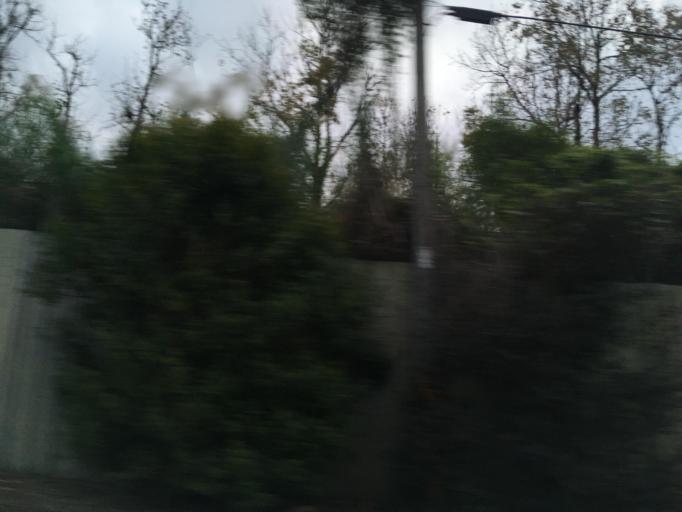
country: TW
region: Taiwan
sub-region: Yilan
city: Yilan
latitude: 24.7475
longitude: 121.7190
